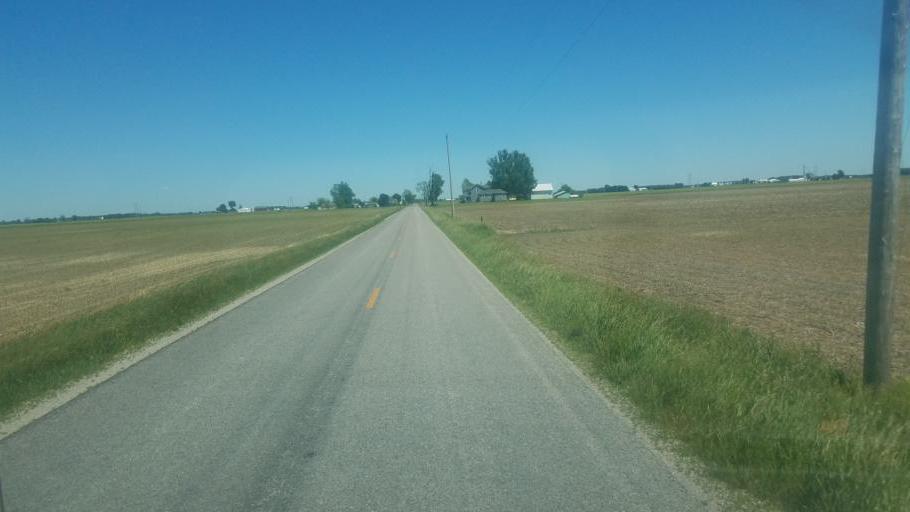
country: US
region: Ohio
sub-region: Shelby County
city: Sidney
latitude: 40.2107
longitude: -84.1108
